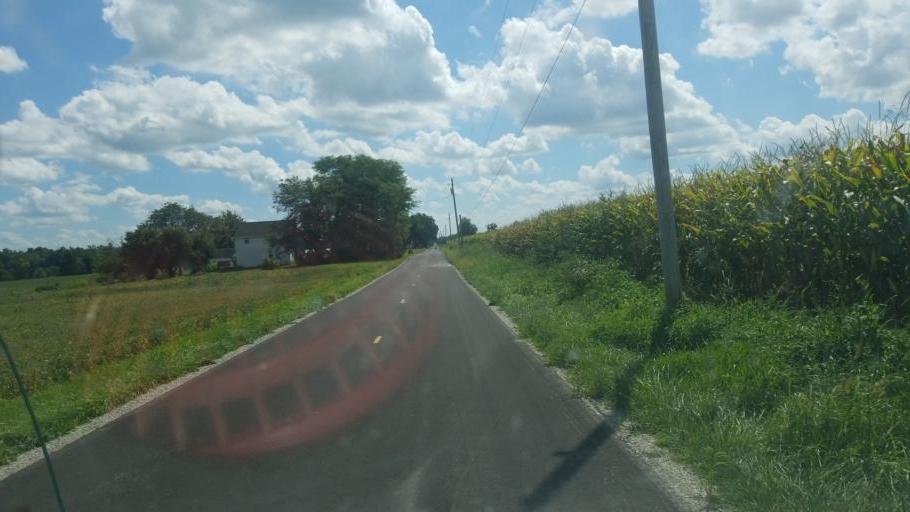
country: US
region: Ohio
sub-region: Marion County
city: Prospect
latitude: 40.5046
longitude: -83.1659
